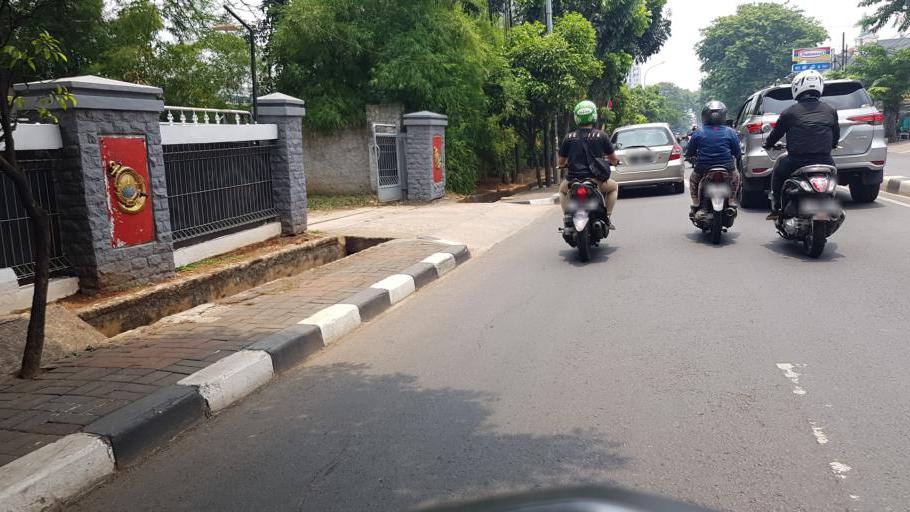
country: ID
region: Jakarta Raya
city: Jakarta
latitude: -6.2977
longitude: 106.8150
